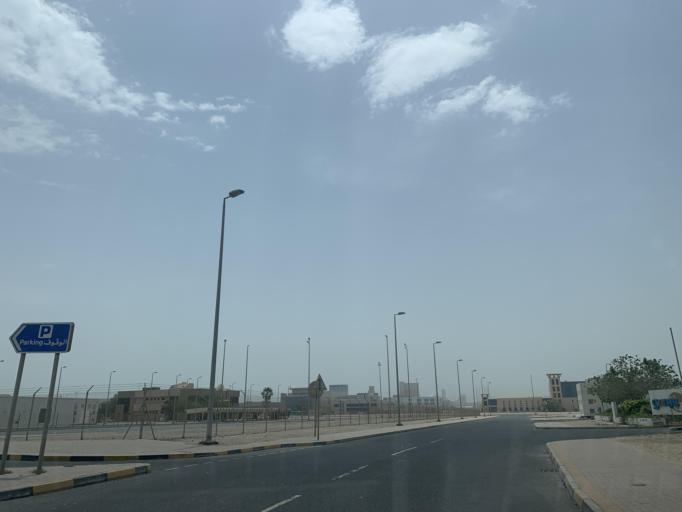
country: BH
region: Muharraq
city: Al Hadd
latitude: 26.2231
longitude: 50.6750
